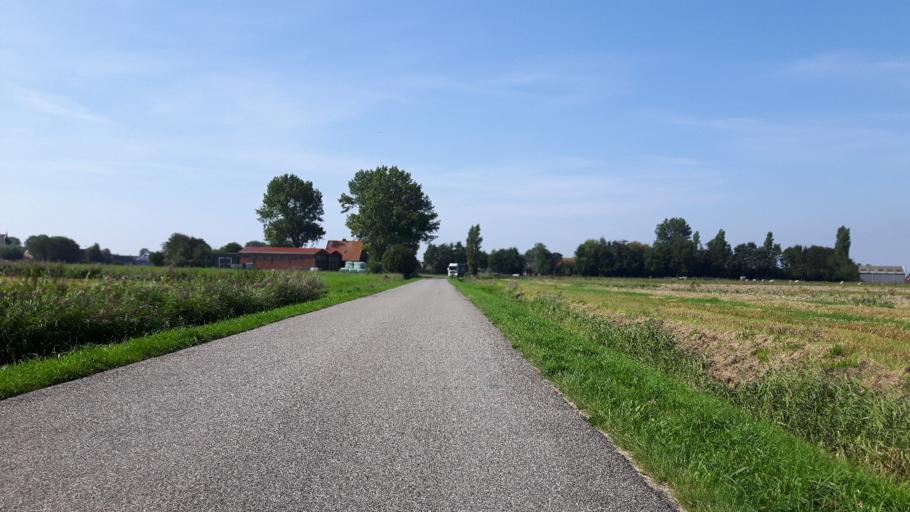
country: NL
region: Friesland
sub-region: Gemeente Dongeradeel
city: Holwerd
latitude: 53.3549
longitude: 5.8672
